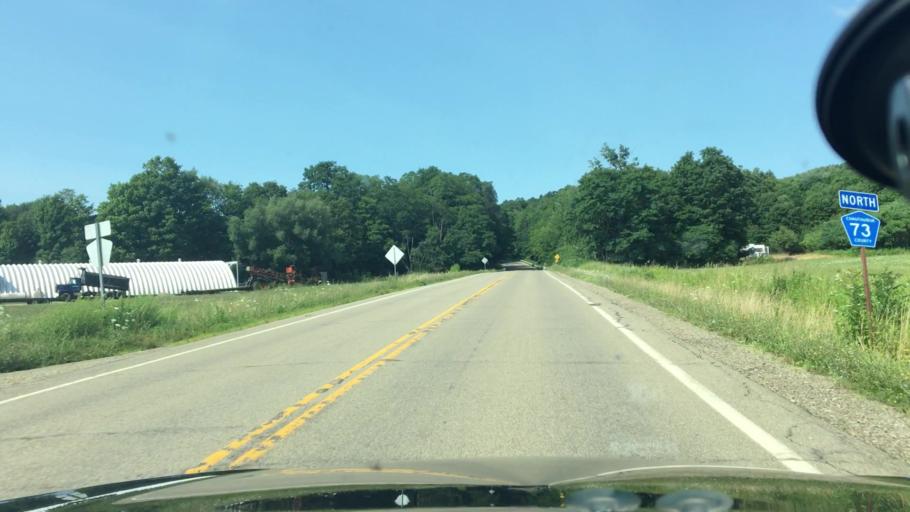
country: US
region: New York
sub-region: Chautauqua County
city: Brocton
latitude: 42.3377
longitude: -79.3665
